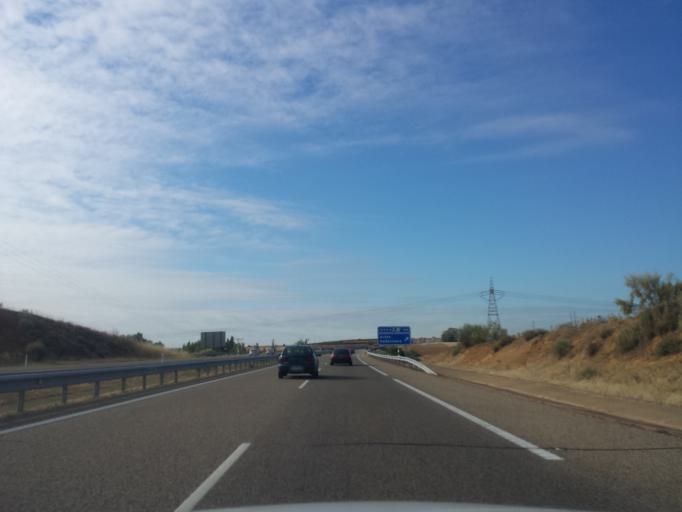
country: ES
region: Castille and Leon
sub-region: Provincia de Leon
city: Ardon
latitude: 42.4546
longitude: -5.5809
